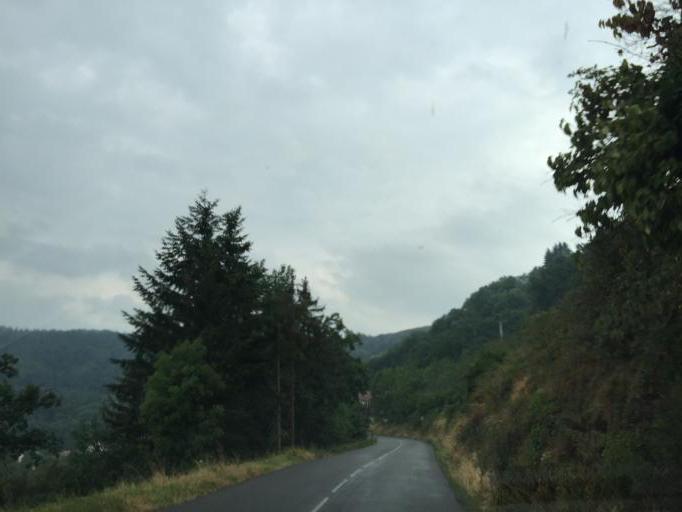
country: FR
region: Rhone-Alpes
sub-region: Departement de la Loire
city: Saint-Christo-en-Jarez
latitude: 45.5257
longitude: 4.4919
